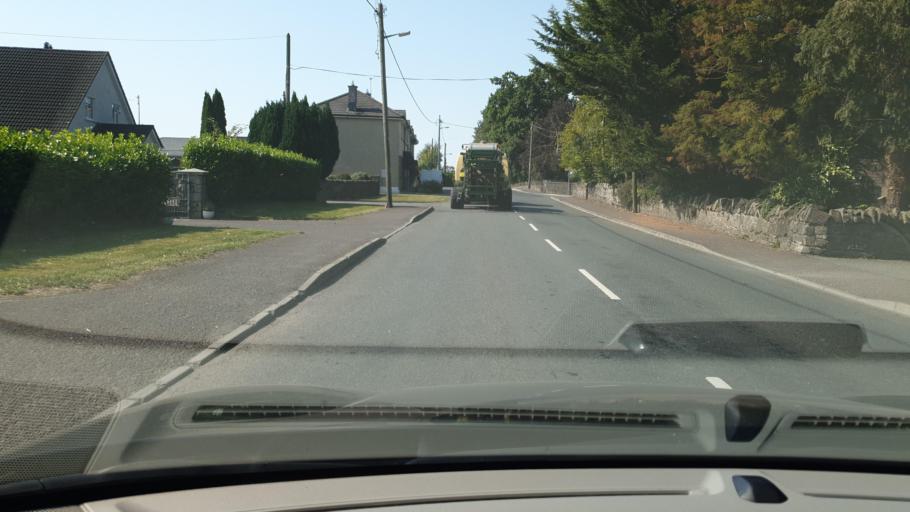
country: IE
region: Leinster
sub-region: An Mhi
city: Athboy
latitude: 53.6213
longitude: -6.9120
